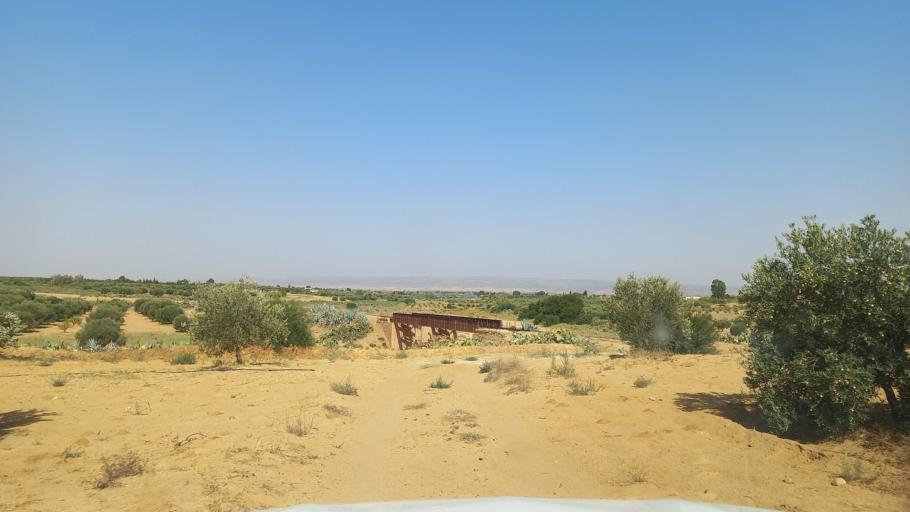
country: TN
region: Al Qasrayn
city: Kasserine
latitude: 35.2272
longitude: 9.0498
